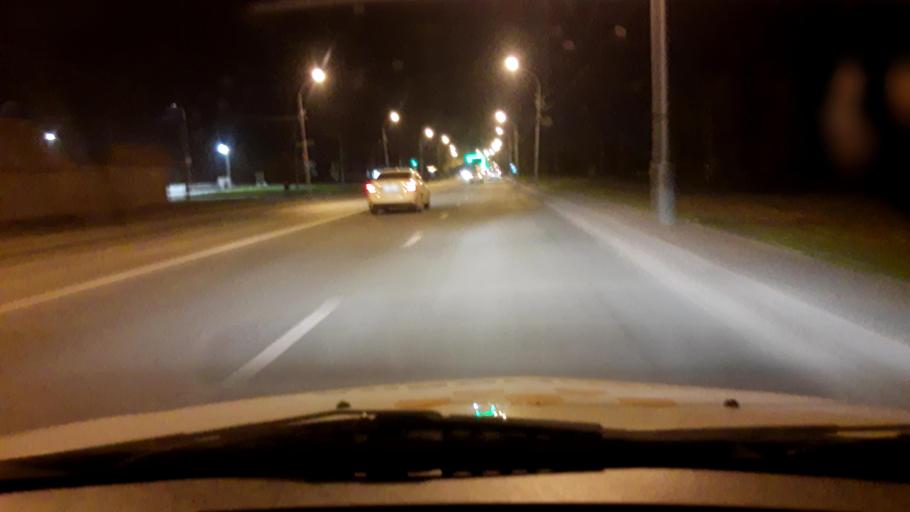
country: RU
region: Bashkortostan
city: Iglino
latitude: 54.7802
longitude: 56.2269
